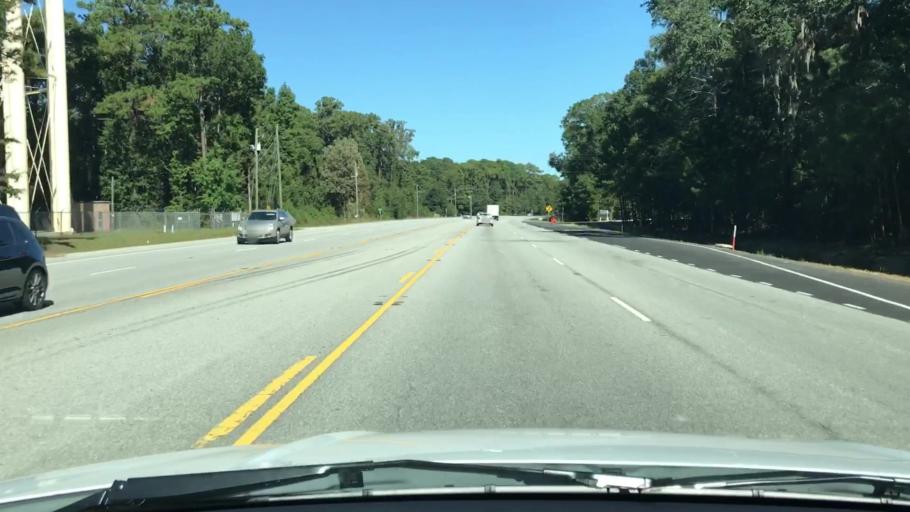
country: US
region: South Carolina
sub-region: Beaufort County
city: Burton
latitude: 32.4142
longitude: -80.7491
